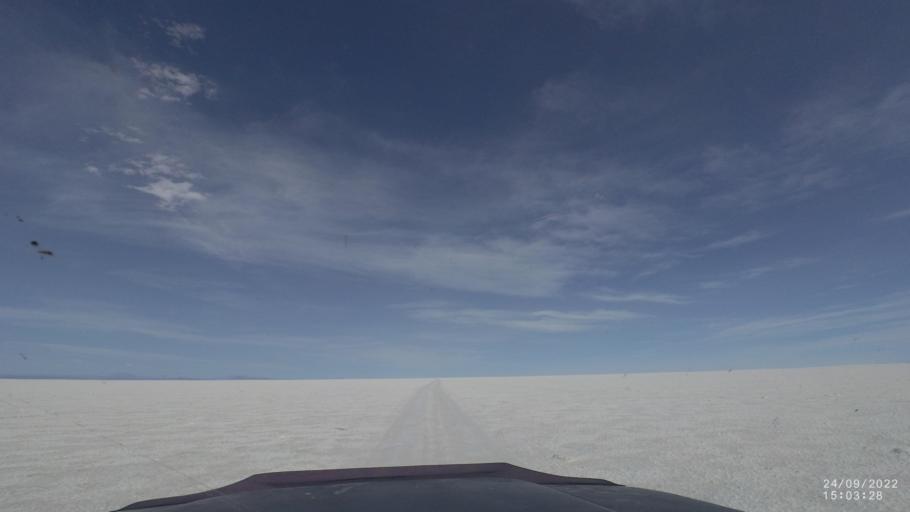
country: BO
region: Potosi
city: Colchani
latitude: -19.8948
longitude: -67.5301
